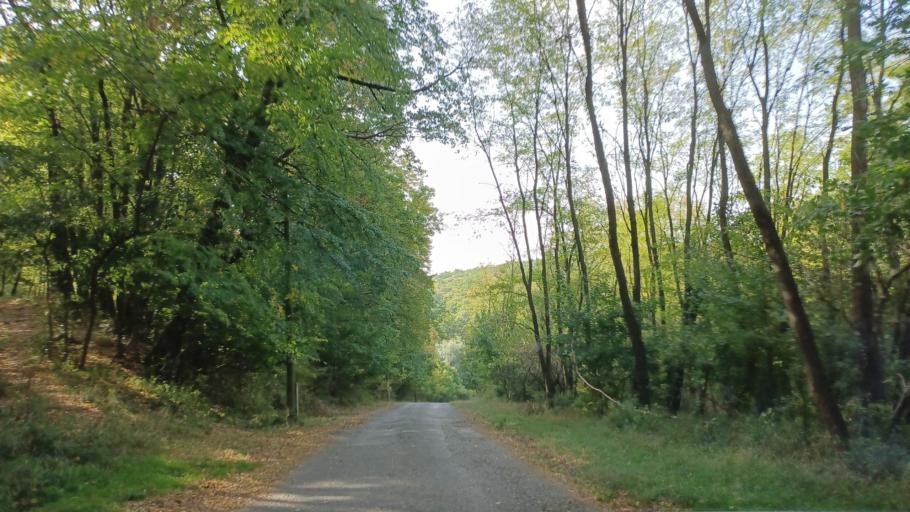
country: HU
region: Baranya
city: Mecseknadasd
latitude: 46.2041
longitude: 18.4531
